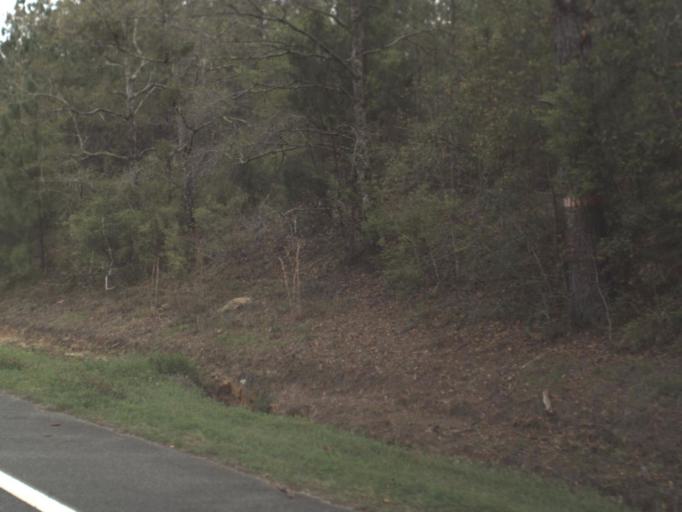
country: US
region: Florida
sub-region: Gulf County
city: Wewahitchka
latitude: 30.2731
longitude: -85.2420
